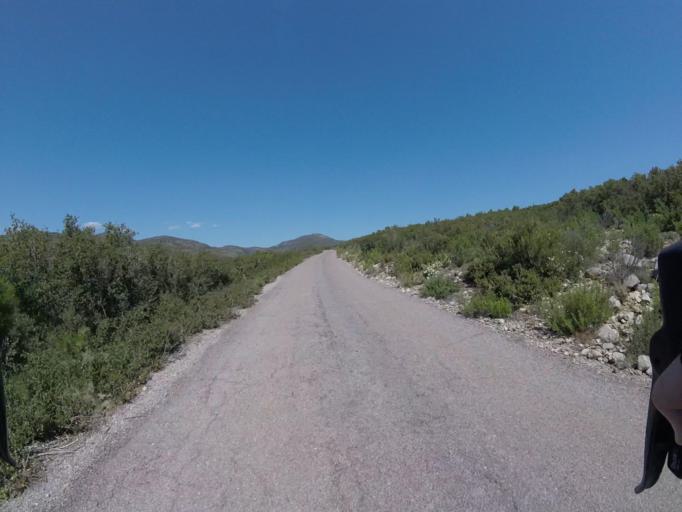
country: ES
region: Valencia
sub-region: Provincia de Castello
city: Sierra-Engarceran
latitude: 40.2374
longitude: -0.0268
